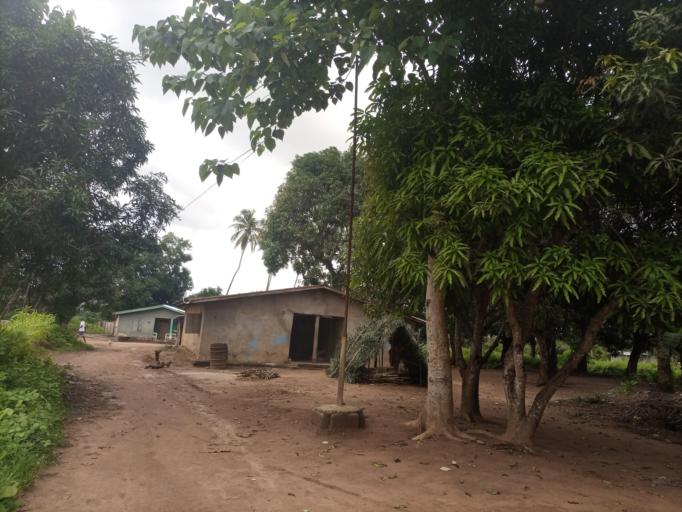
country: SL
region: Northern Province
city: Masoyila
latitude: 8.5937
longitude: -13.1640
